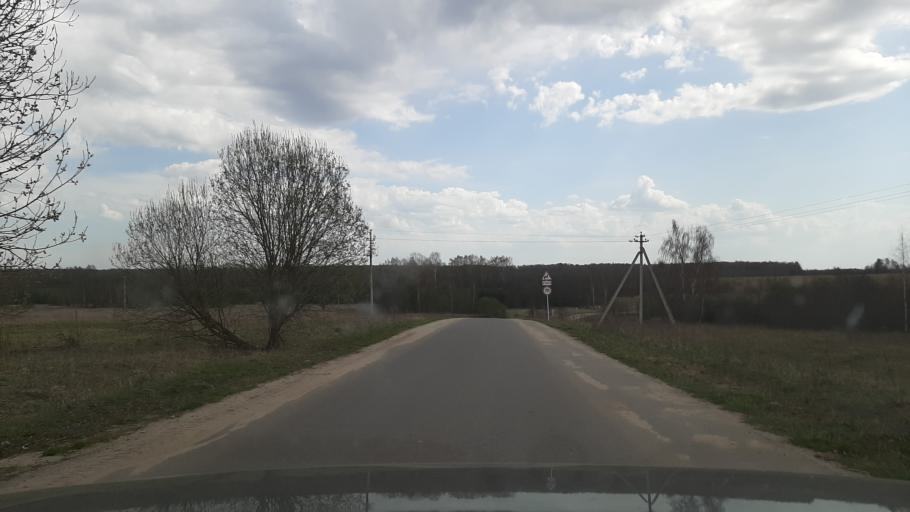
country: RU
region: Ivanovo
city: Furmanov
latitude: 57.3180
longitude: 41.1651
